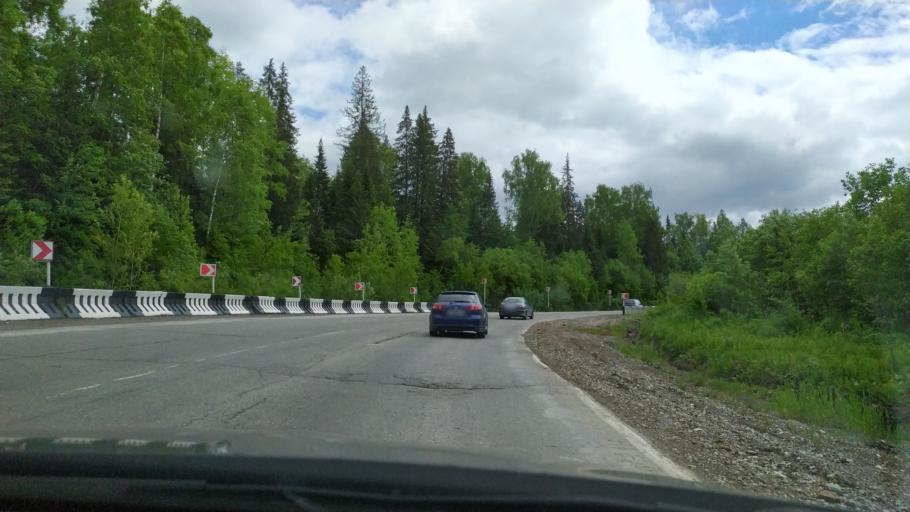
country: RU
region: Perm
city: Gremyachinsk
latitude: 58.4418
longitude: 57.8863
